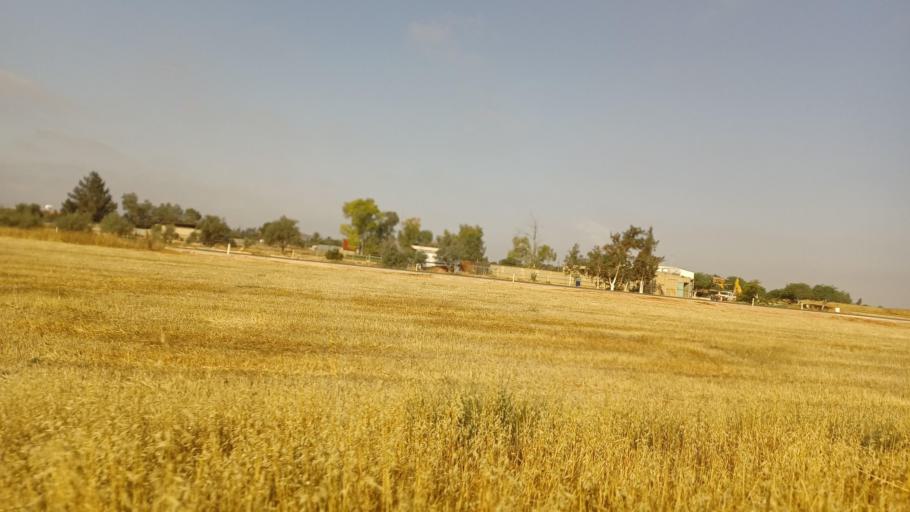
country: CY
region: Ammochostos
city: Avgorou
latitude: 35.0498
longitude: 33.8211
